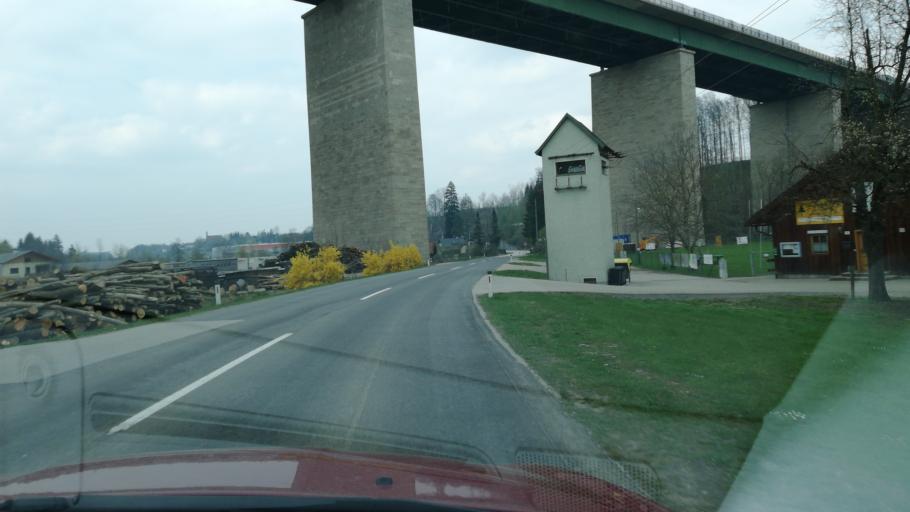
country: AT
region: Upper Austria
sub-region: Politischer Bezirk Vocklabruck
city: Attnang-Puchheim
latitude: 47.9603
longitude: 13.7461
